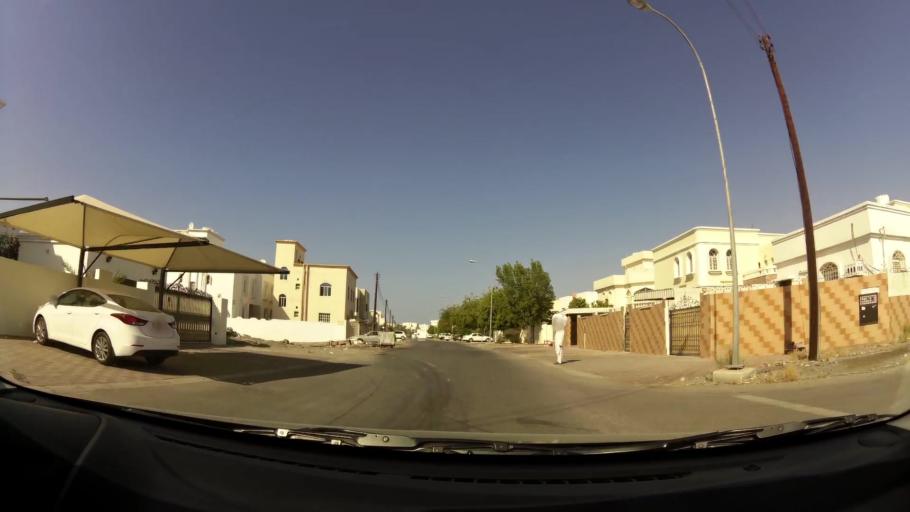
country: OM
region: Muhafazat Masqat
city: As Sib al Jadidah
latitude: 23.6204
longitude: 58.2030
